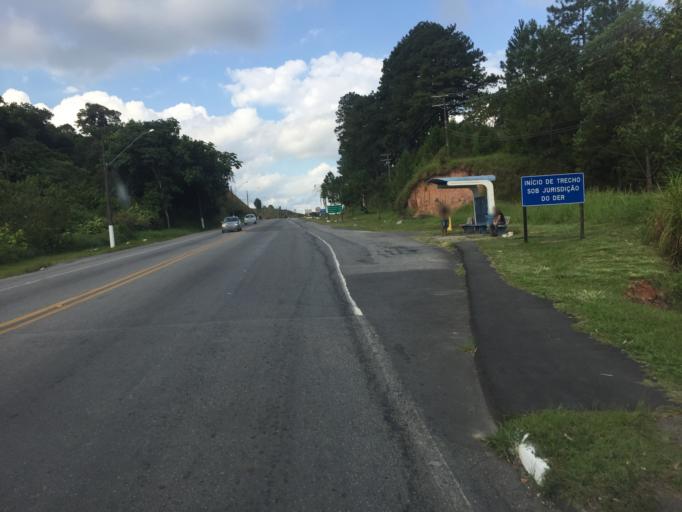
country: BR
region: Sao Paulo
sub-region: Aruja
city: Aruja
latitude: -23.4041
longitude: -46.3148
